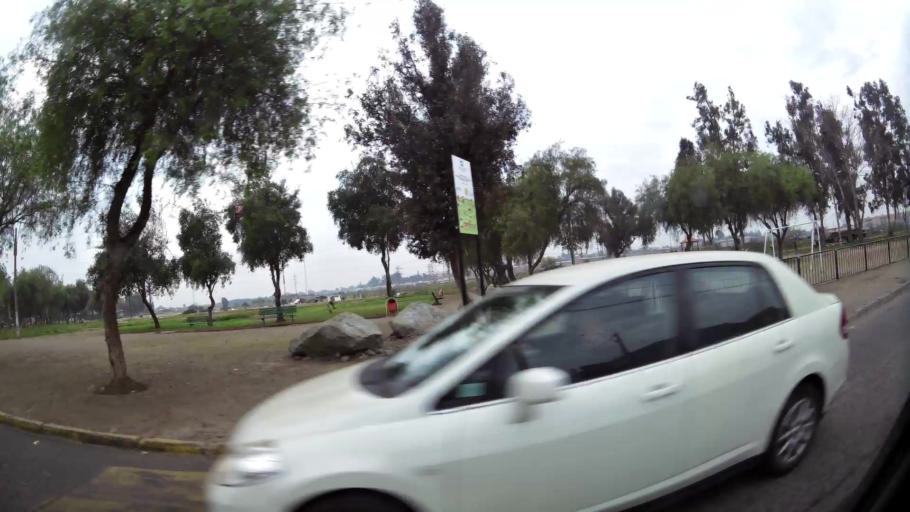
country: CL
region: Santiago Metropolitan
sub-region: Provincia de Santiago
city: Lo Prado
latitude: -33.4817
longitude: -70.7331
